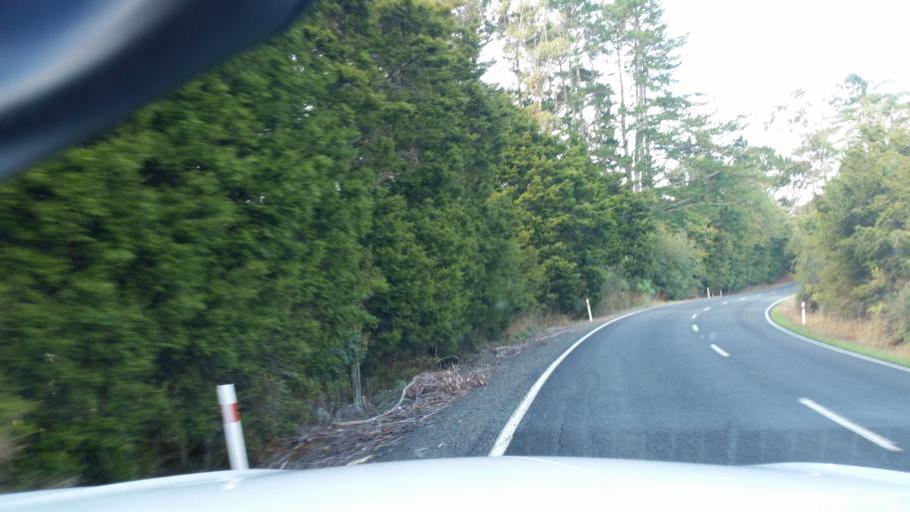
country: NZ
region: Northland
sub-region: Whangarei
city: Ruakaka
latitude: -35.9856
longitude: 174.2935
